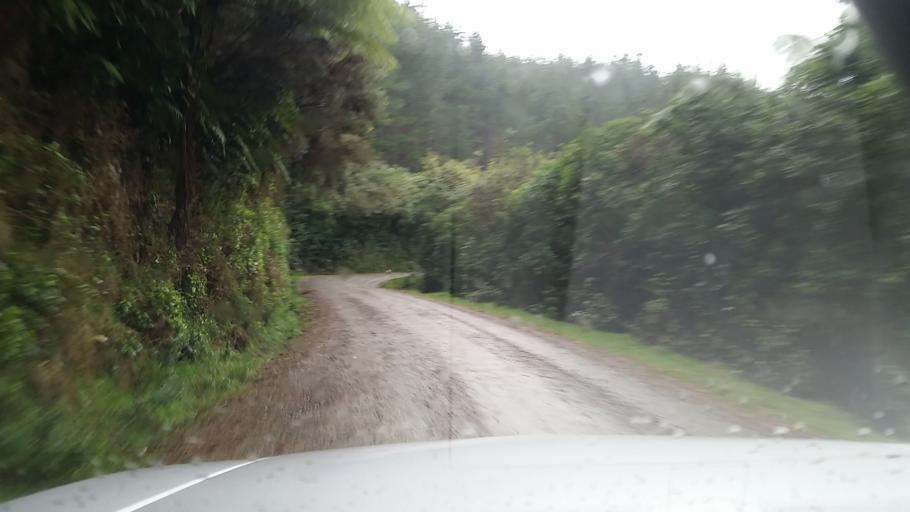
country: NZ
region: Marlborough
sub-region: Marlborough District
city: Picton
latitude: -41.1388
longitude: 174.0527
